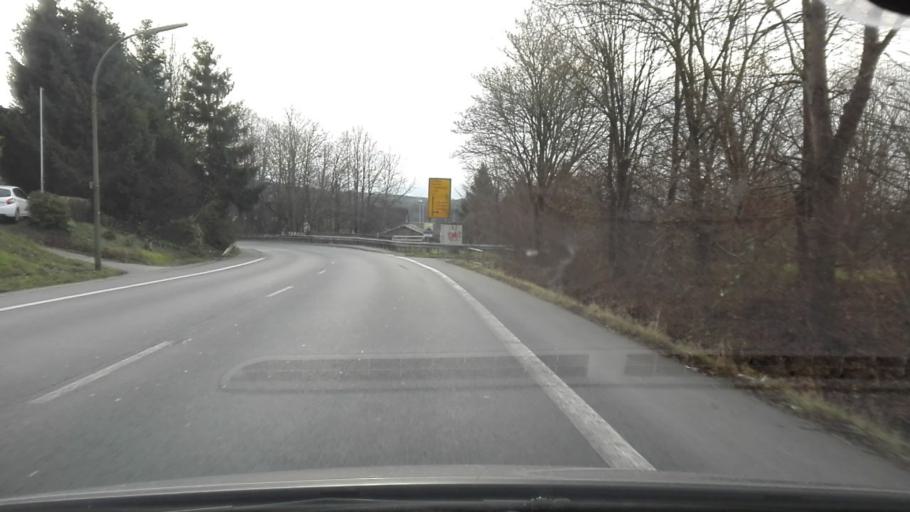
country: DE
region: North Rhine-Westphalia
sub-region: Regierungsbezirk Arnsberg
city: Frondenberg
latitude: 51.4768
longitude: 7.7076
